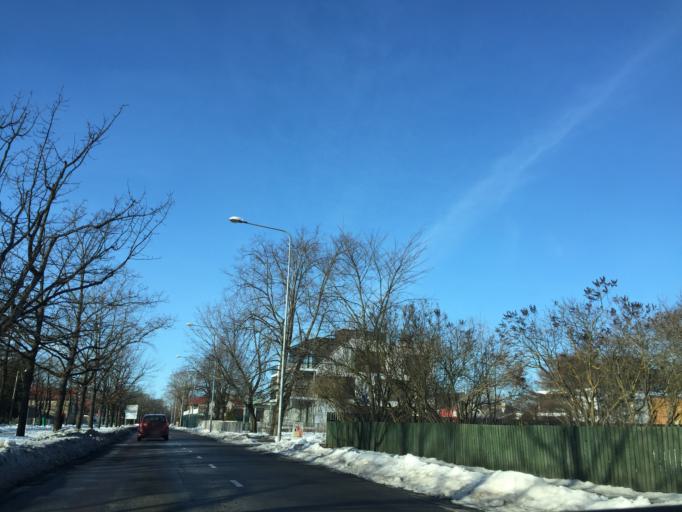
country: EE
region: Paernumaa
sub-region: Paernu linn
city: Parnu
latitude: 58.3756
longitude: 24.5084
